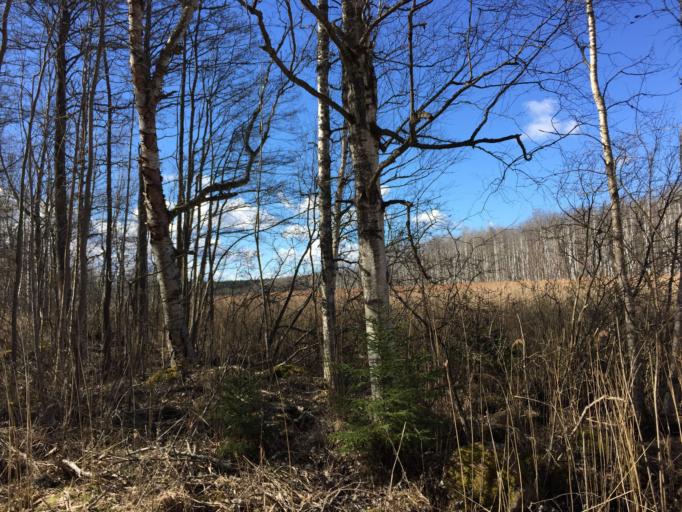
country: SE
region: OEstergoetland
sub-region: Finspangs Kommun
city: Finspang
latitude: 58.8828
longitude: 15.7695
